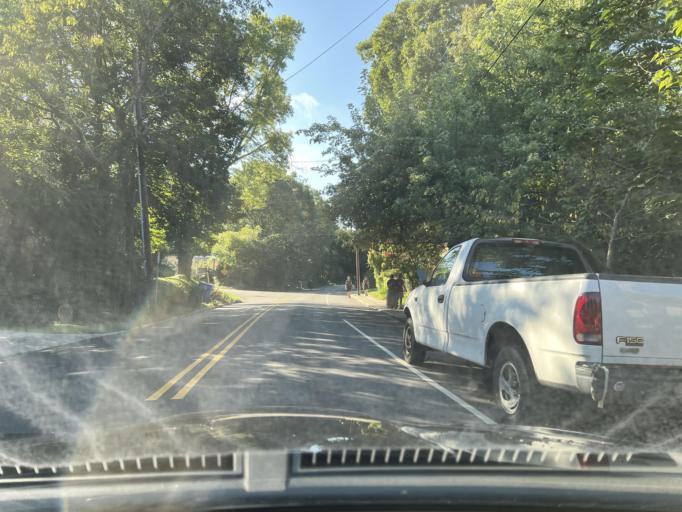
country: US
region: North Carolina
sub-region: Buncombe County
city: Asheville
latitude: 35.5758
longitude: -82.5853
